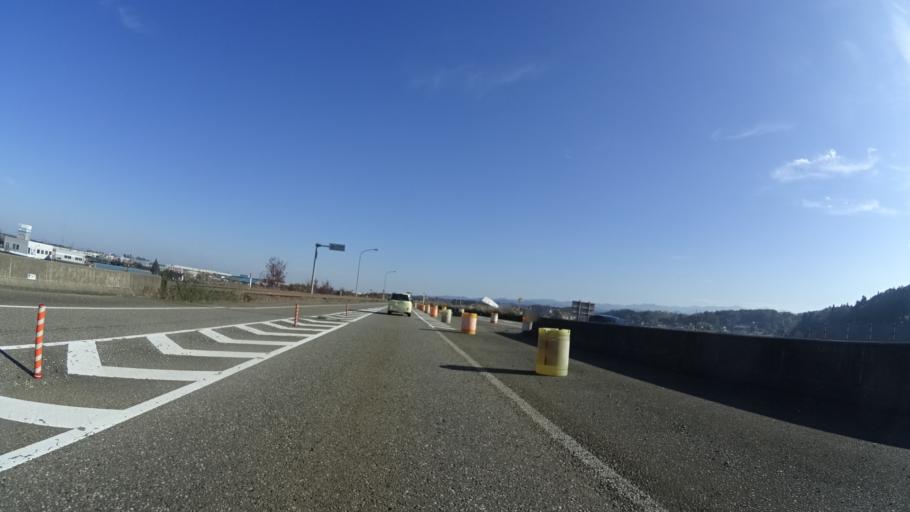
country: JP
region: Ishikawa
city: Komatsu
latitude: 36.3286
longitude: 136.4149
